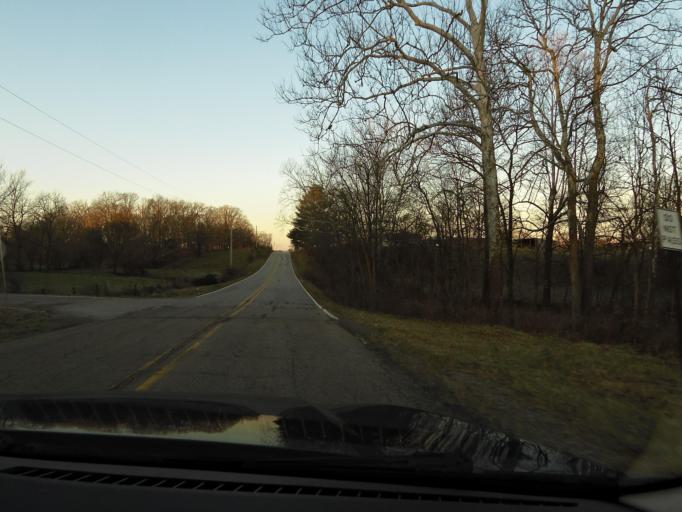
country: US
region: Illinois
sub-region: Marion County
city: Salem
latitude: 38.7588
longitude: -88.9008
